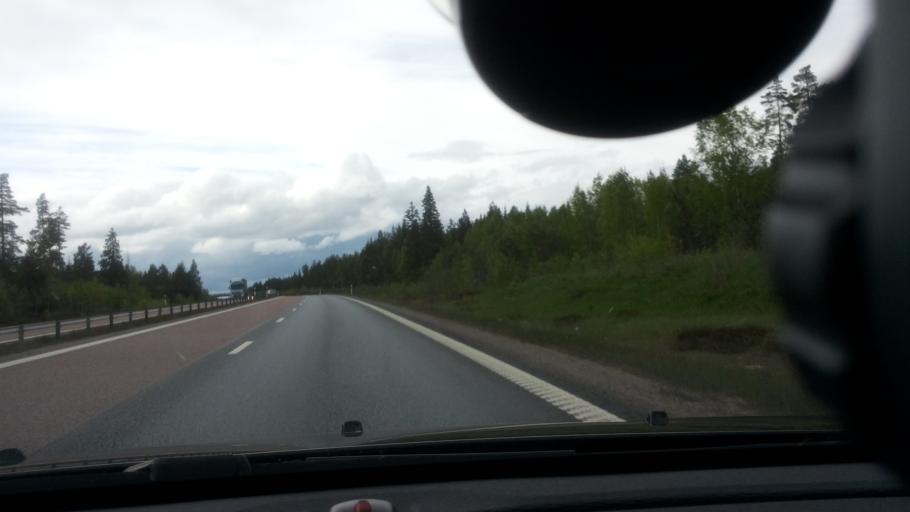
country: SE
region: Gaevleborg
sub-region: Soderhamns Kommun
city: Soderhamn
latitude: 61.3672
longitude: 17.0097
